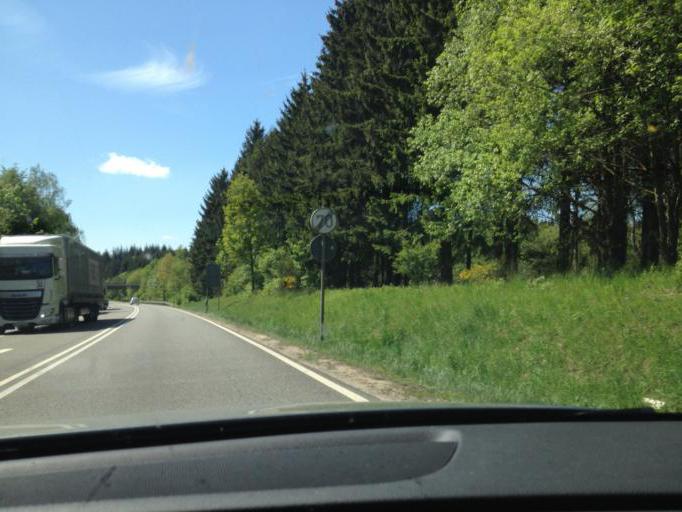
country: DE
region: North Rhine-Westphalia
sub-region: Regierungsbezirk Koln
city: Blankenheim
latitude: 50.4510
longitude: 6.6621
